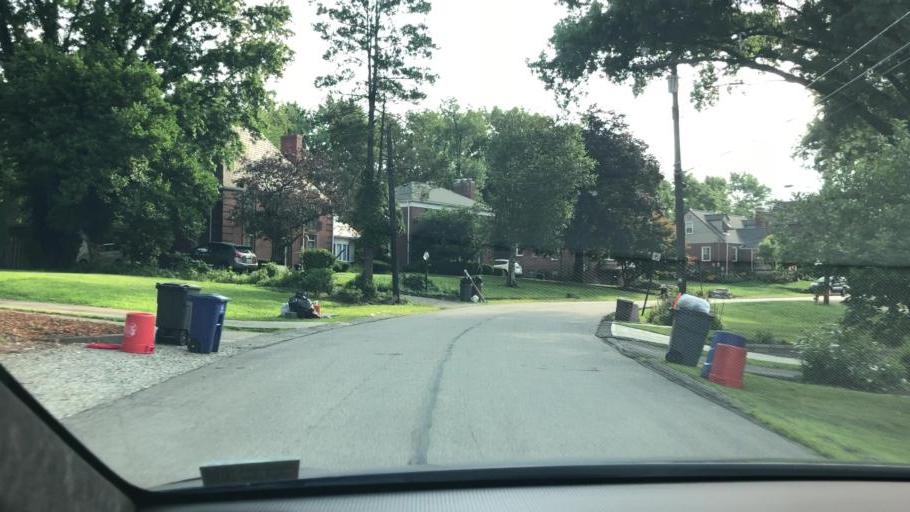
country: US
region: Pennsylvania
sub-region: Allegheny County
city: Penn Hills
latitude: 40.4727
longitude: -79.8259
